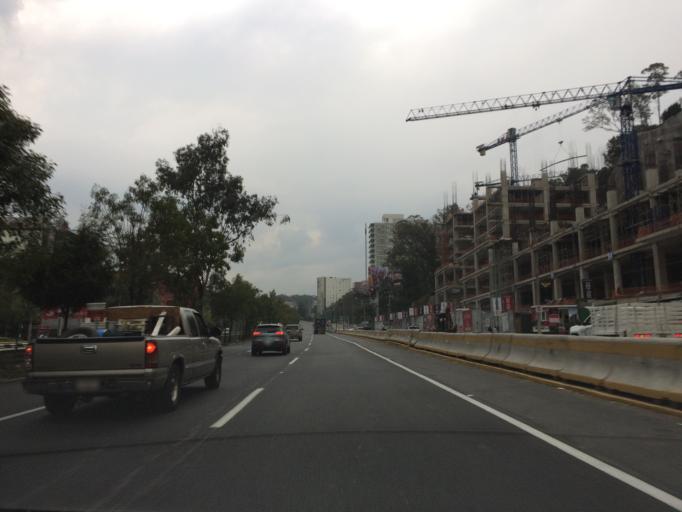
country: MX
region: Mexico City
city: Col. Bosques de las Lomas
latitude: 19.3782
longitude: -99.2553
